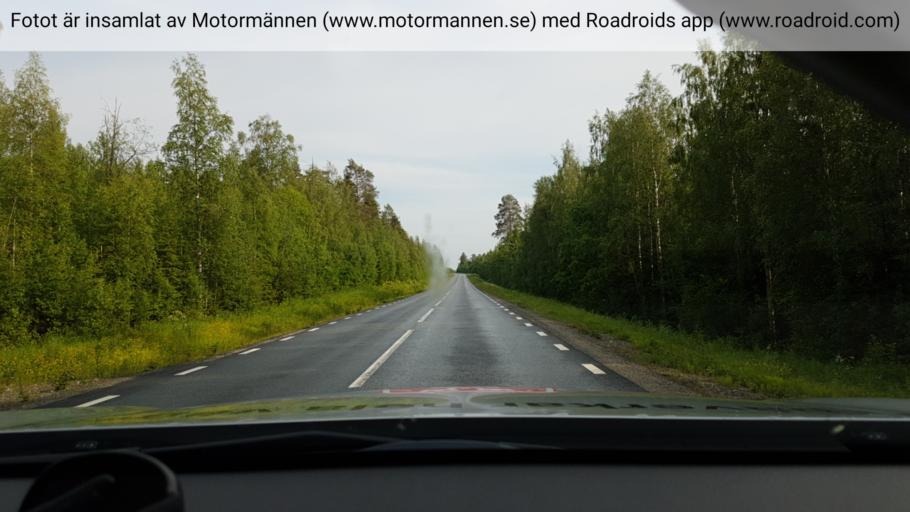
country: SE
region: Vaesterbotten
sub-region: Bjurholms Kommun
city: Bjurholm
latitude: 64.3302
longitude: 19.1531
